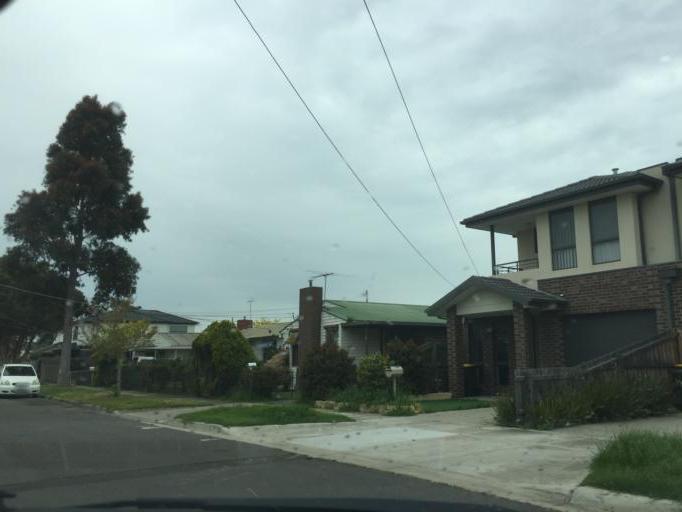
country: AU
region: Victoria
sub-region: Brimbank
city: Sunshine North
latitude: -37.7808
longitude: 144.8364
